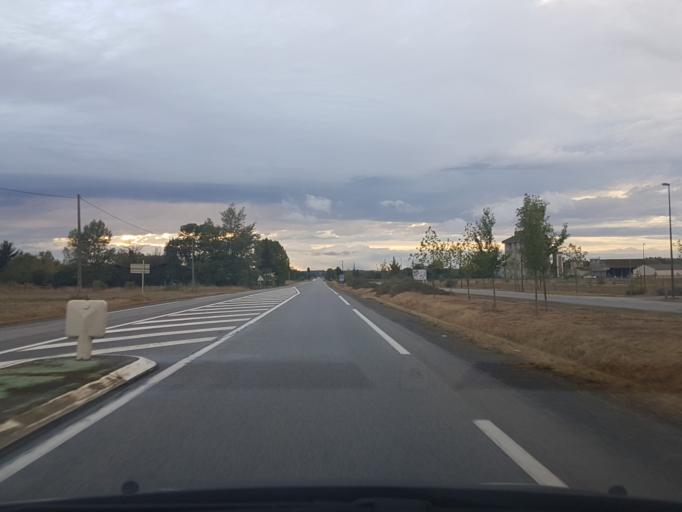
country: FR
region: Midi-Pyrenees
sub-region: Departement de l'Ariege
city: Mirepoix
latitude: 43.0729
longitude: 1.7927
